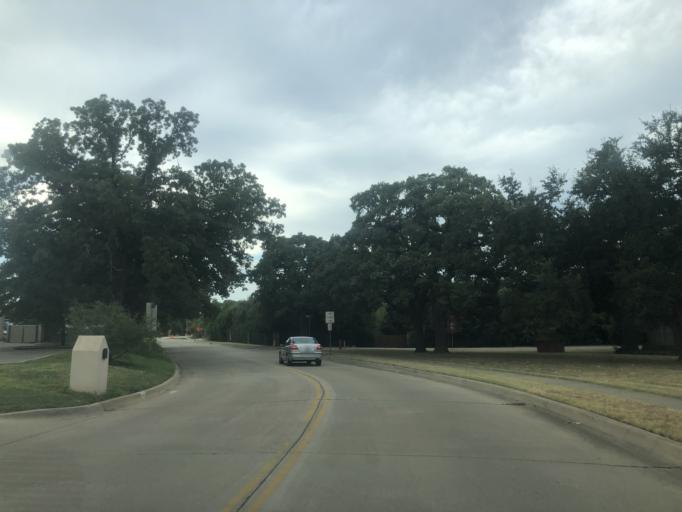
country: US
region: Texas
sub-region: Tarrant County
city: Colleyville
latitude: 32.8789
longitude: -97.1606
